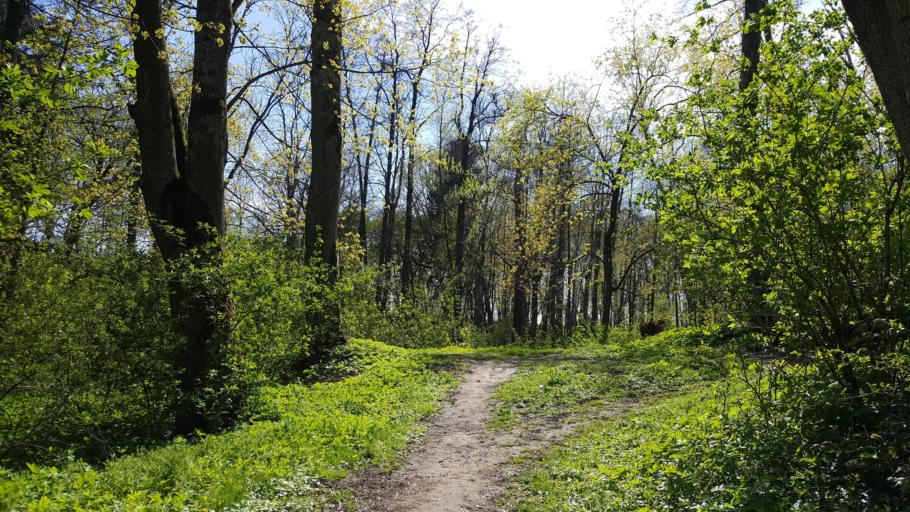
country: BY
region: Brest
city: Vysokaye
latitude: 52.3651
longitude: 23.3721
